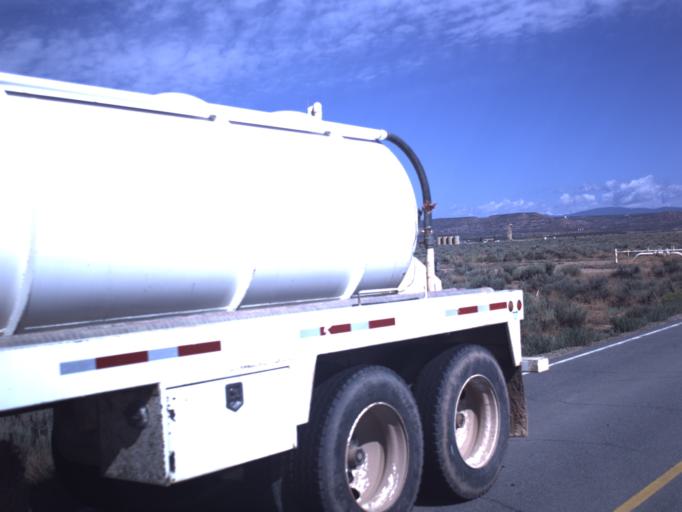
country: US
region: Utah
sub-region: Duchesne County
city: Duchesne
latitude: 40.2342
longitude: -110.3893
